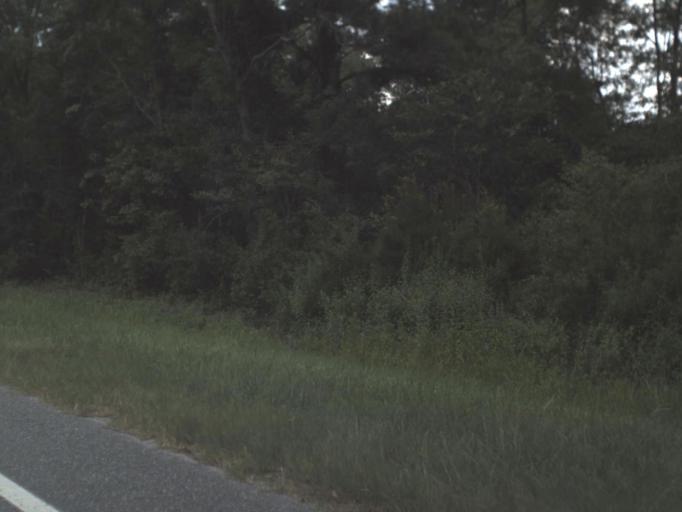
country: US
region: Florida
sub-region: Hamilton County
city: Jasper
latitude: 30.5659
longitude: -83.0743
